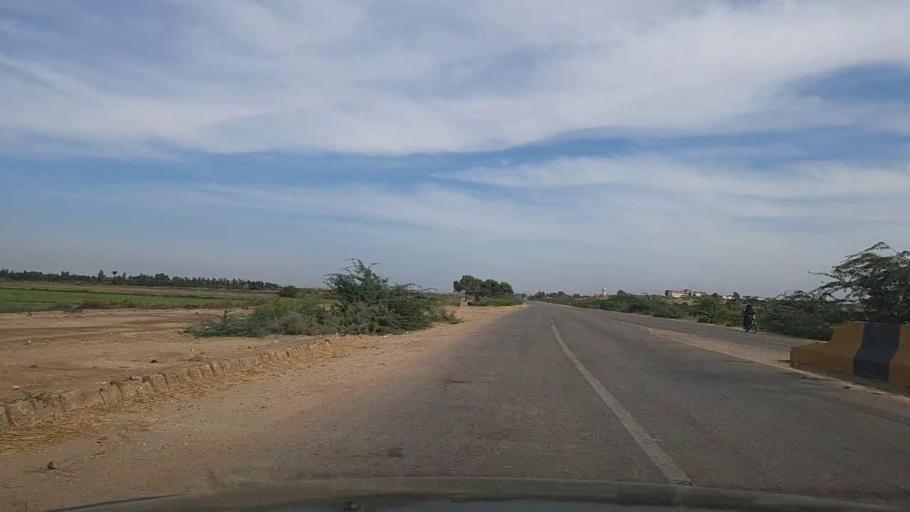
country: PK
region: Sindh
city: Thatta
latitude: 24.8133
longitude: 67.9781
